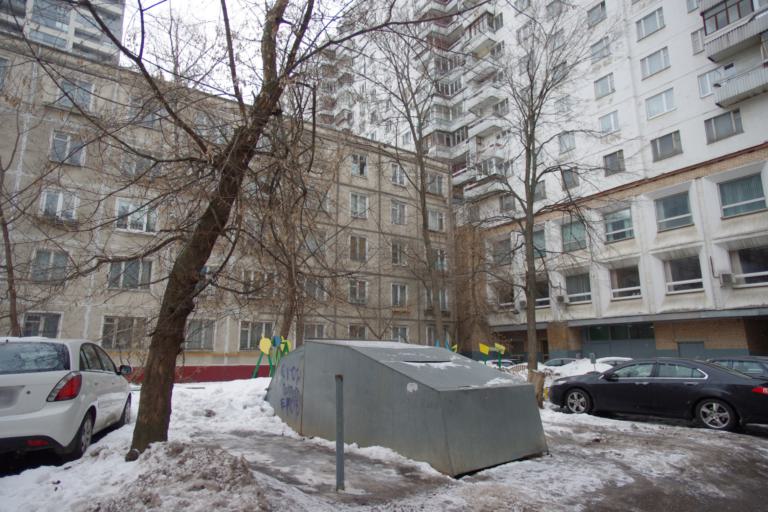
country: RU
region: Moskovskaya
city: Khoroshevo-Mnevniki
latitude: 55.7746
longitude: 37.4713
